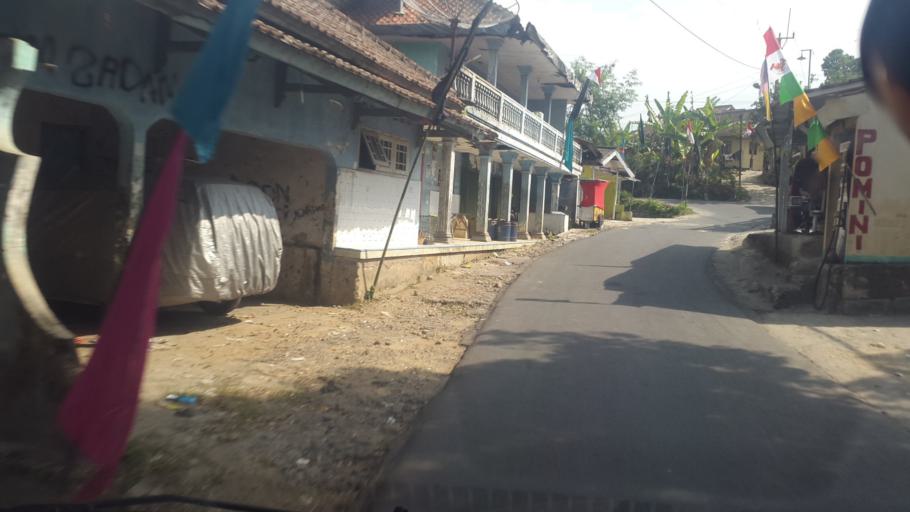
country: ID
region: West Java
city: Cicurug
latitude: -6.7776
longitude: 106.7288
